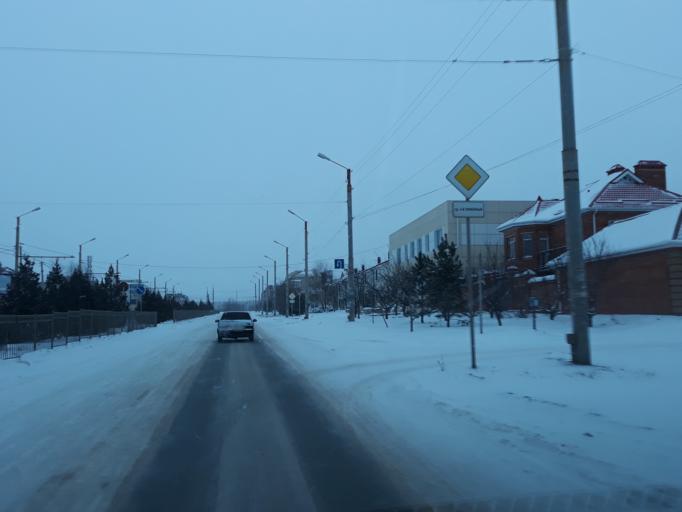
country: RU
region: Rostov
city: Taganrog
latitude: 47.2741
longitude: 38.9180
